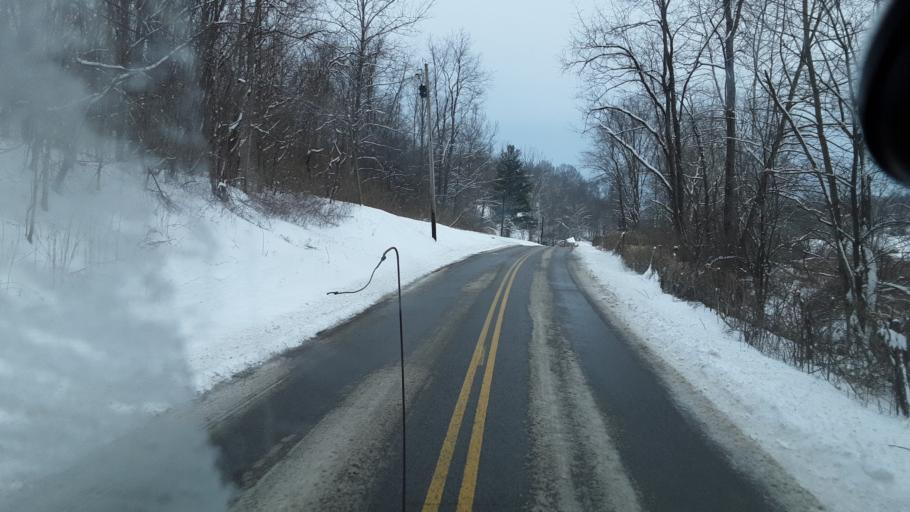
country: US
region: Ohio
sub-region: Perry County
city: Somerset
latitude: 39.9025
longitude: -82.2277
